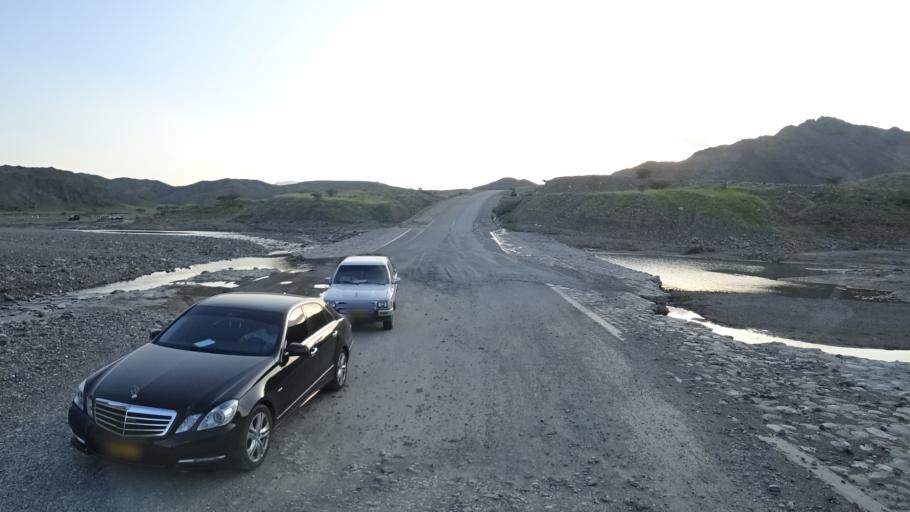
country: OM
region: Al Batinah
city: Al Khaburah
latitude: 23.7985
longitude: 56.9876
